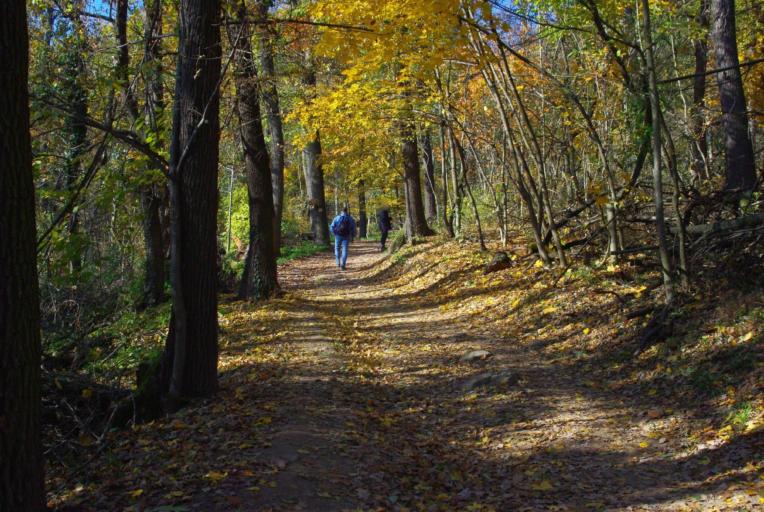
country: HU
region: Pest
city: Budakeszi
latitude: 47.5322
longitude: 18.9582
